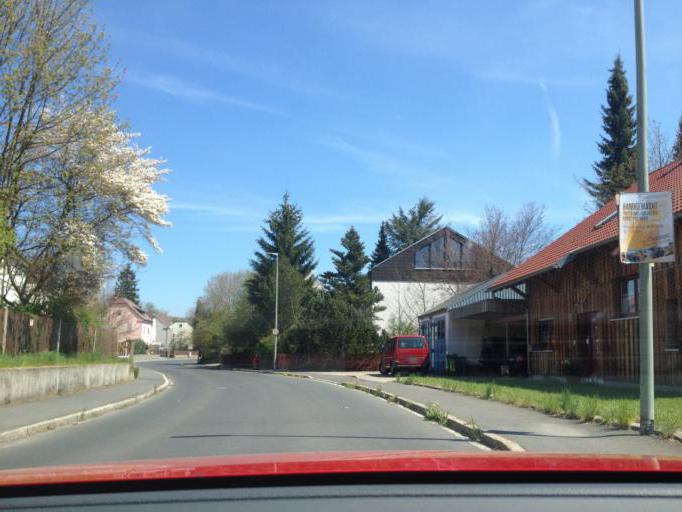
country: DE
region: Bavaria
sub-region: Upper Franconia
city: Marktleuthen
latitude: 50.1294
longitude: 12.0021
